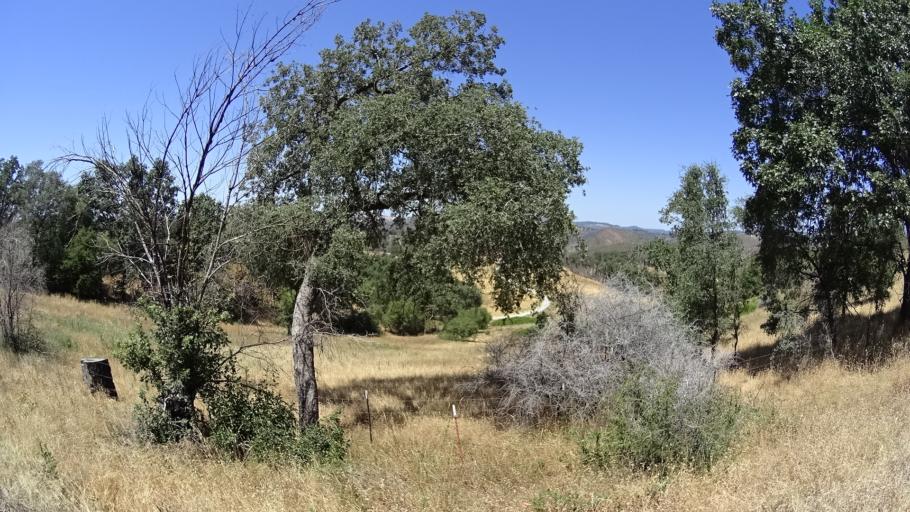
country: US
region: California
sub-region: Calaveras County
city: Mountain Ranch
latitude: 38.2923
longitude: -120.6191
